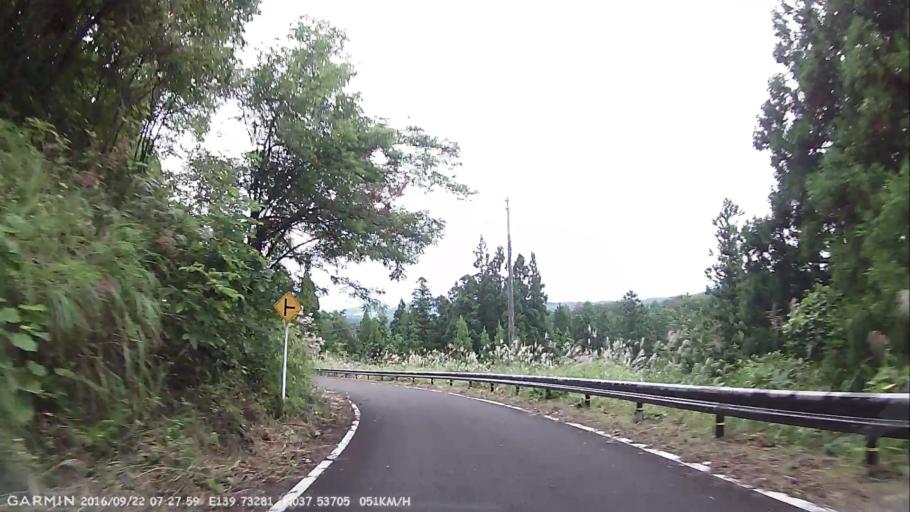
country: JP
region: Fukushima
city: Kitakata
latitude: 37.5372
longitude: 139.7329
